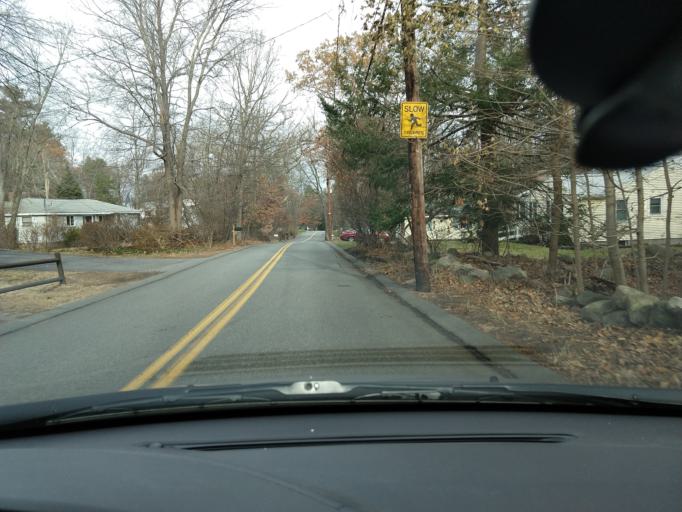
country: US
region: Massachusetts
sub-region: Middlesex County
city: Bedford
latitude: 42.4970
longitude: -71.2486
